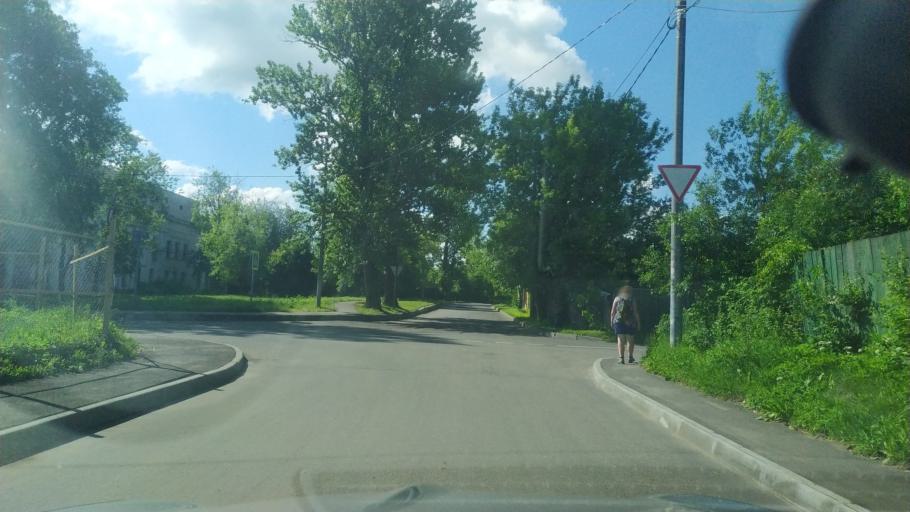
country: RU
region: Moscow
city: Vostochnyy
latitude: 55.8154
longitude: 37.8656
